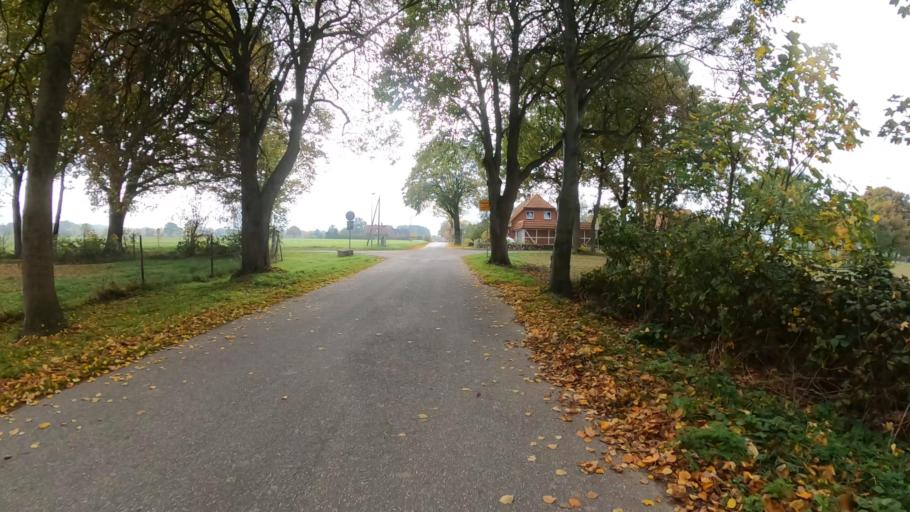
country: DE
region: Lower Saxony
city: Neu Wulmstorf
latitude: 53.4278
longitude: 9.8014
